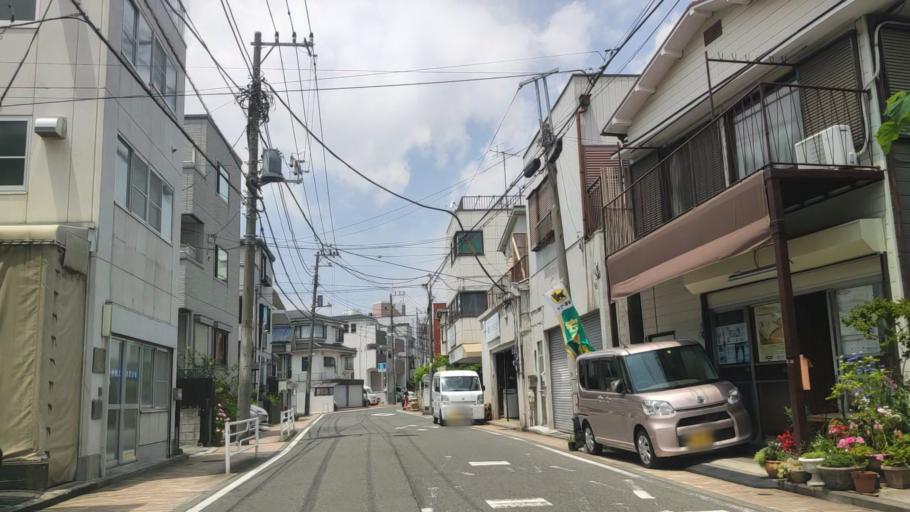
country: JP
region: Kanagawa
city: Yokohama
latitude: 35.4303
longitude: 139.6575
